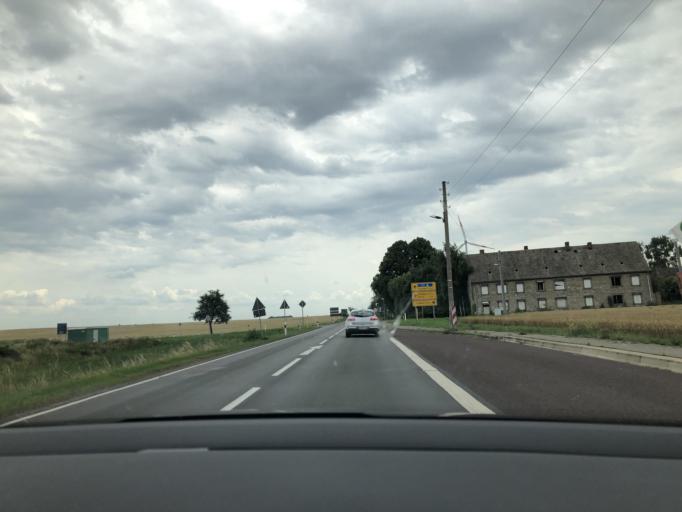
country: DE
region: Saxony-Anhalt
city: Unseburg
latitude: 51.9345
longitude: 11.5355
